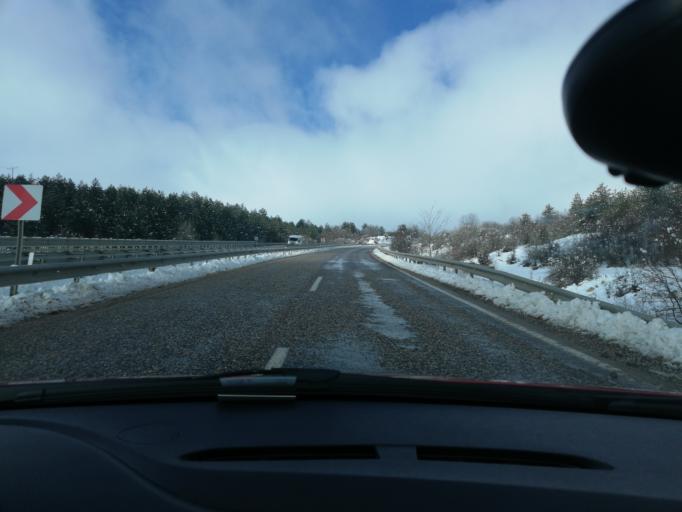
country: TR
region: Kastamonu
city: Ihsangazi
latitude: 41.3049
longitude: 33.5840
